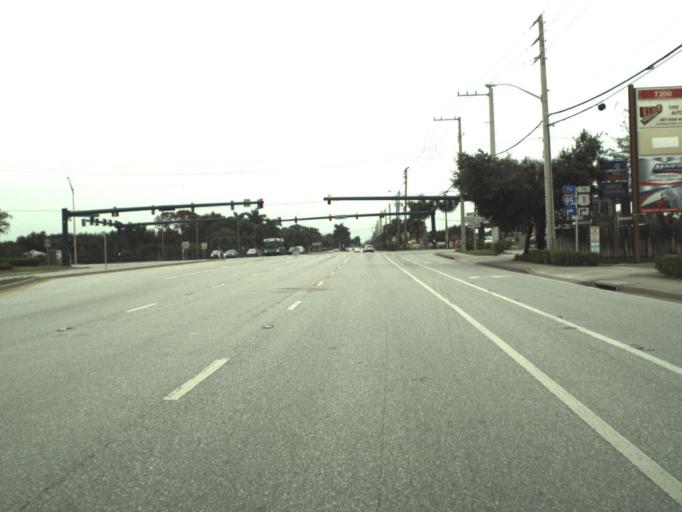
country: US
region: Florida
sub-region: Palm Beach County
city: Mangonia Park
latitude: 26.7823
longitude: -80.1072
